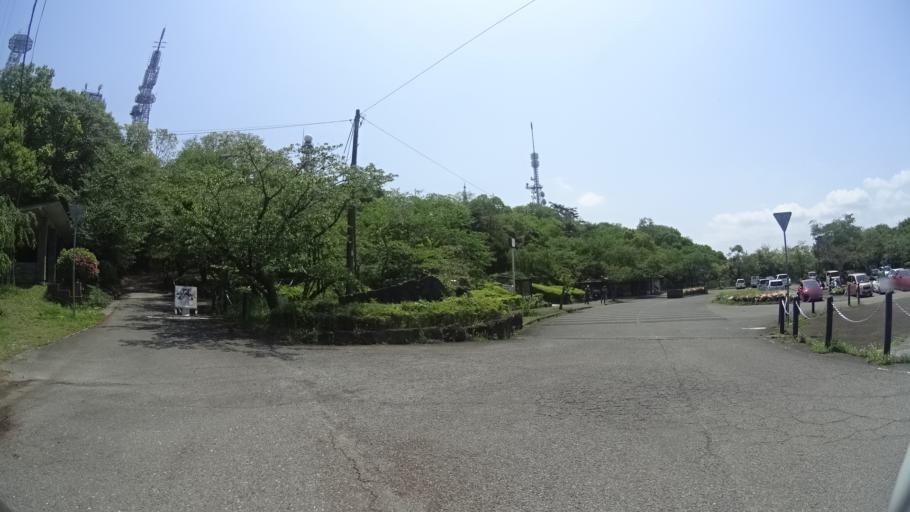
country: JP
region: Tokushima
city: Tokushima-shi
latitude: 34.0678
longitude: 134.5362
